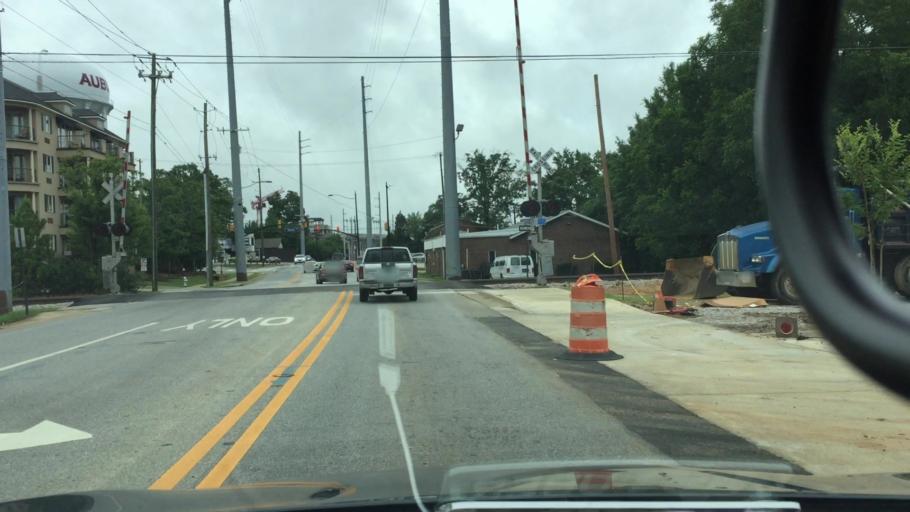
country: US
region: Alabama
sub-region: Lee County
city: Auburn
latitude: 32.6103
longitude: -85.4904
